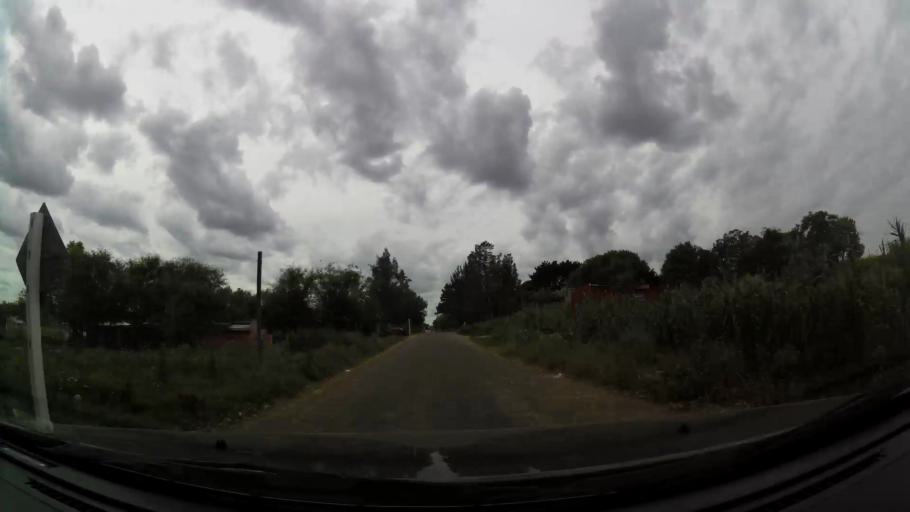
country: UY
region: Canelones
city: Las Piedras
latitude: -34.7126
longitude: -56.2048
